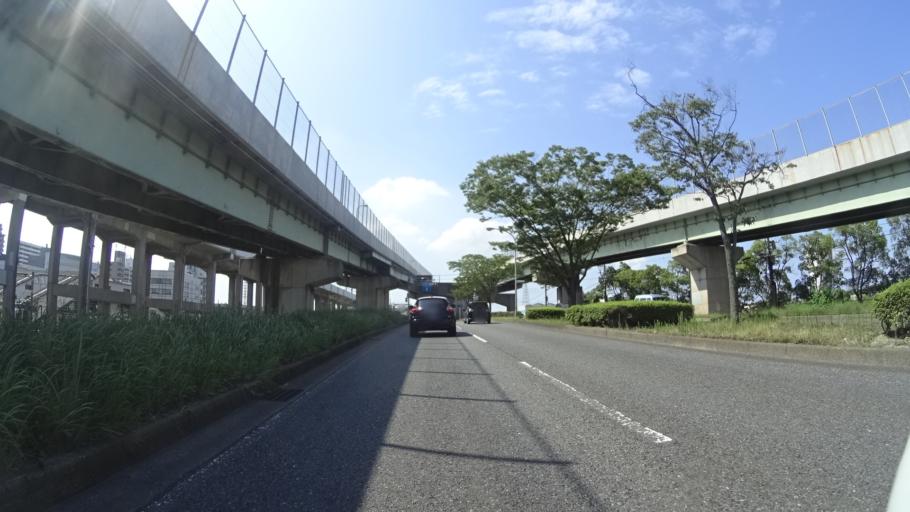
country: JP
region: Fukuoka
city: Kitakyushu
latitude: 33.8891
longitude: 130.8749
